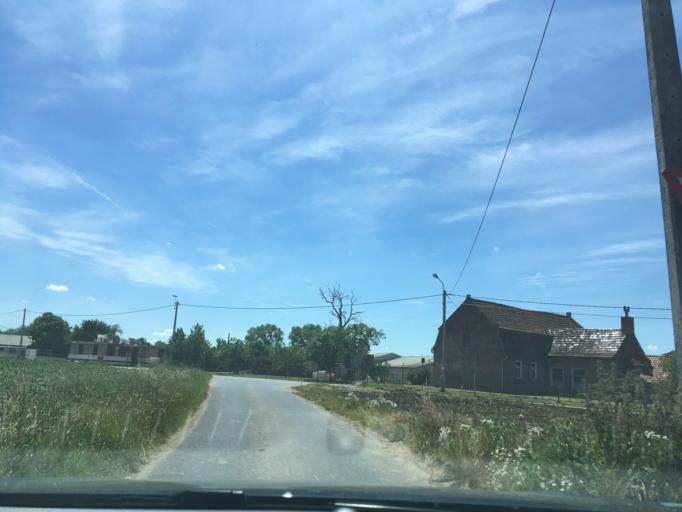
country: BE
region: Flanders
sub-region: Provincie West-Vlaanderen
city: Hooglede
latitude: 51.0030
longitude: 3.0925
